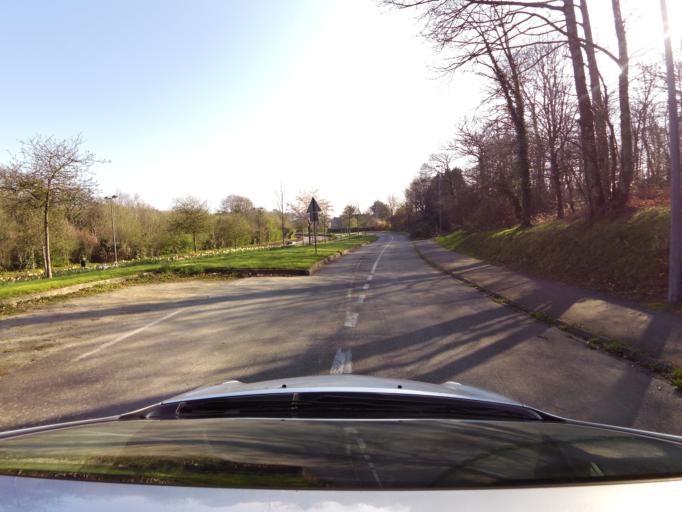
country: FR
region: Brittany
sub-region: Departement du Morbihan
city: Gestel
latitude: 47.7967
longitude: -3.4820
